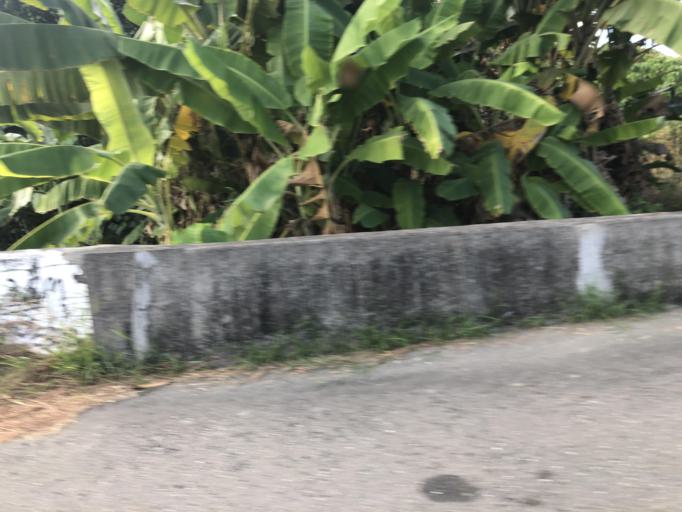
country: TW
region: Taiwan
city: Yujing
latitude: 23.0474
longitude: 120.4239
